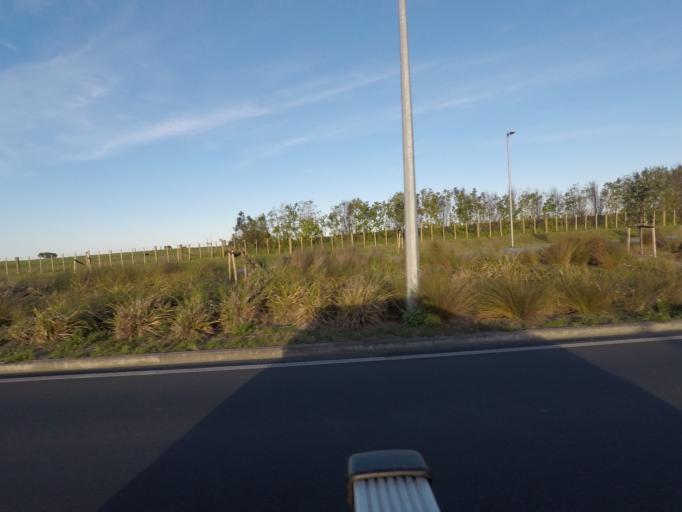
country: NZ
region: Auckland
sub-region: Auckland
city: Rosebank
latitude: -36.8550
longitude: 174.6515
